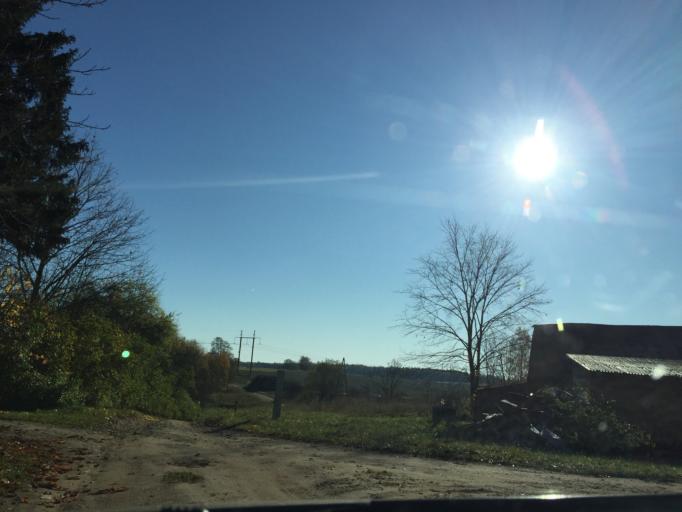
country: LV
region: Skriveri
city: Skriveri
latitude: 56.6707
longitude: 25.1647
